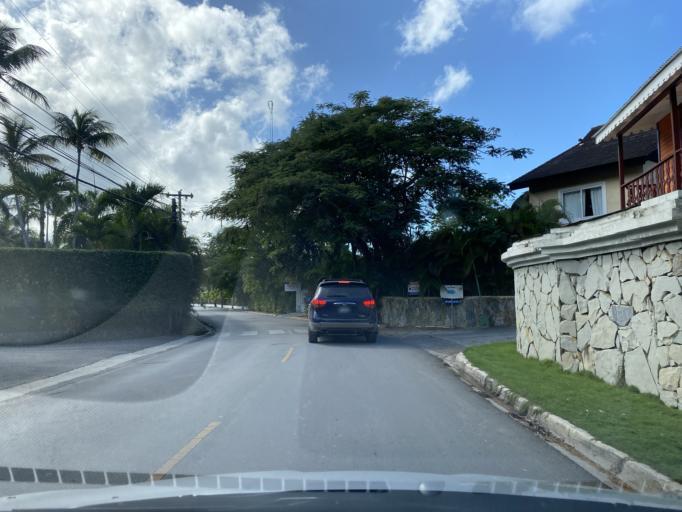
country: DO
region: Samana
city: Las Terrenas
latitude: 19.3124
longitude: -69.5665
